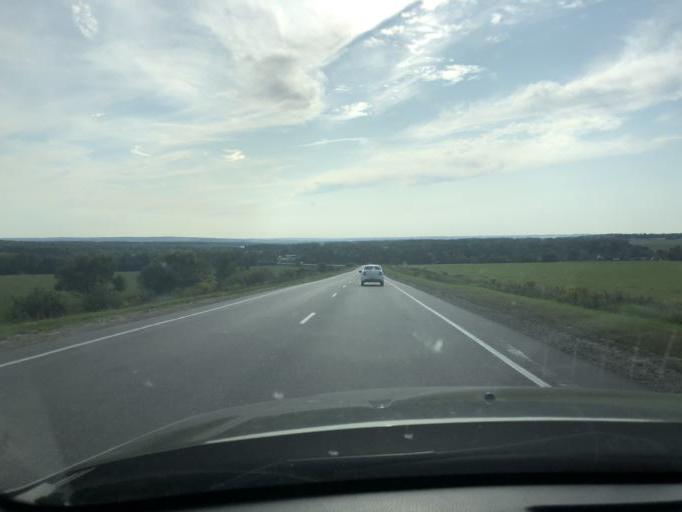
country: RU
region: Tula
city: Krapivna
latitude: 54.1204
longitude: 37.2348
